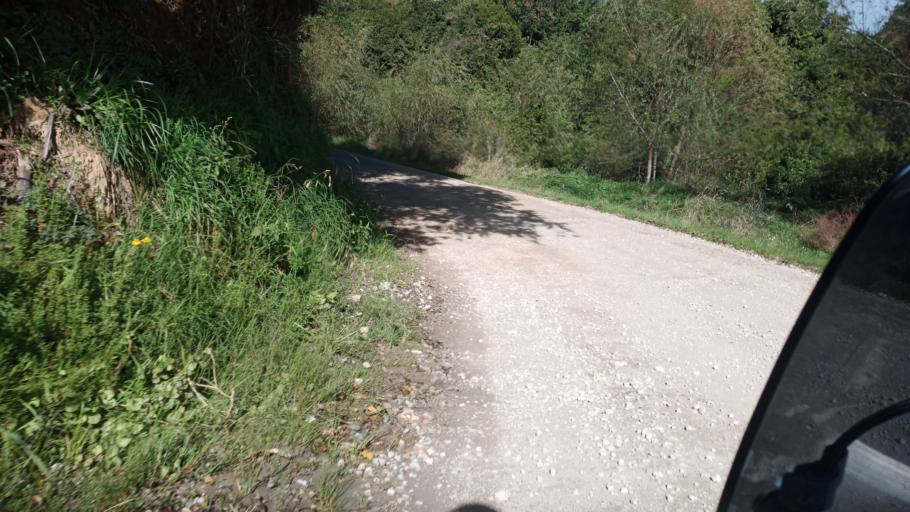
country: NZ
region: Gisborne
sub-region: Gisborne District
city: Gisborne
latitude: -38.5384
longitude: 177.5188
